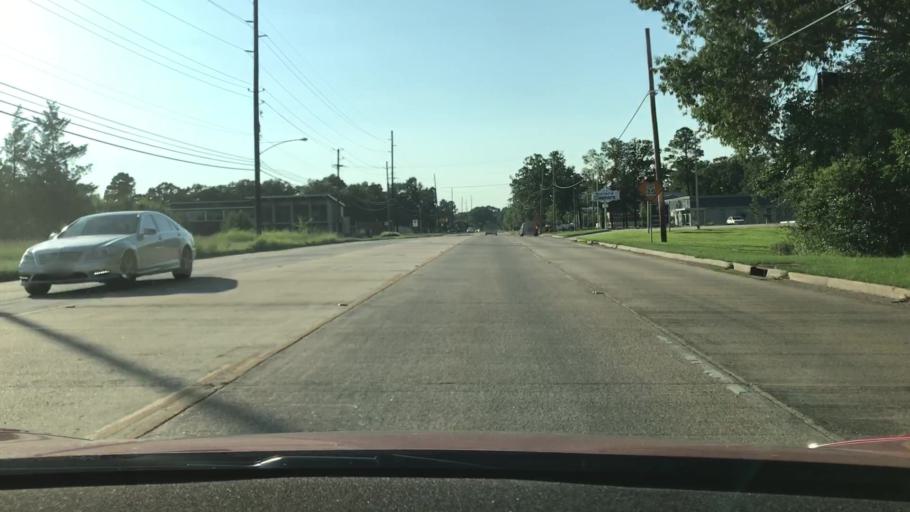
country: US
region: Louisiana
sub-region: Bossier Parish
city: Bossier City
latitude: 32.4266
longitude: -93.7410
